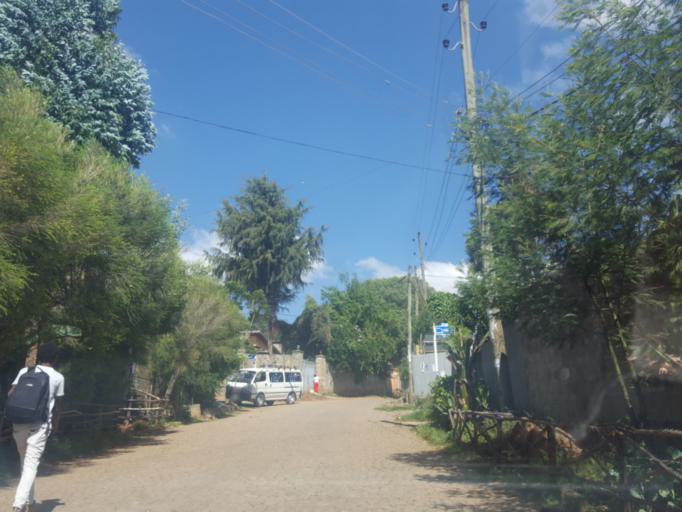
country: ET
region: Adis Abeba
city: Addis Ababa
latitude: 9.0598
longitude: 38.7414
